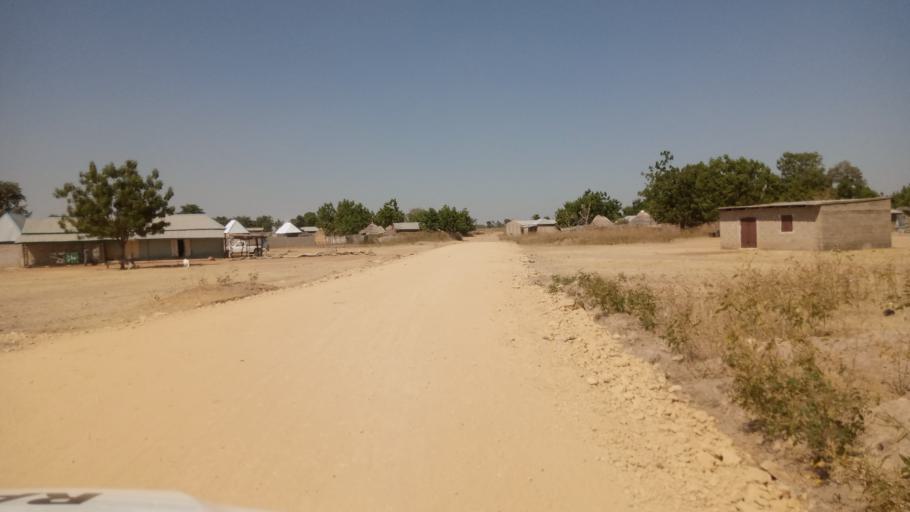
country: NG
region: Adamawa
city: Ngurore
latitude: 9.2978
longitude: 12.1375
